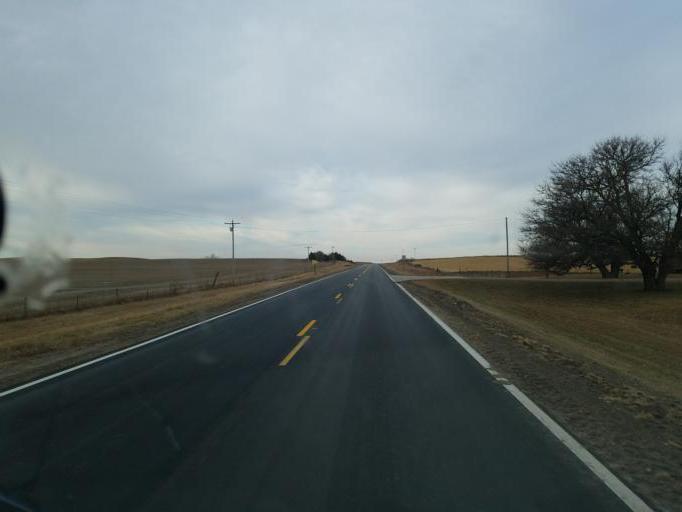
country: US
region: Nebraska
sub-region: Knox County
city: Center
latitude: 42.5970
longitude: -97.8089
